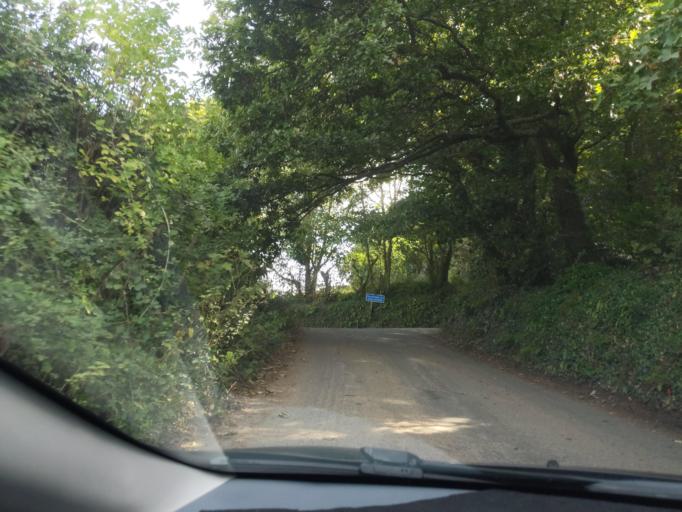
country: GB
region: England
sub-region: Cornwall
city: Torpoint
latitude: 50.3578
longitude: -4.2352
